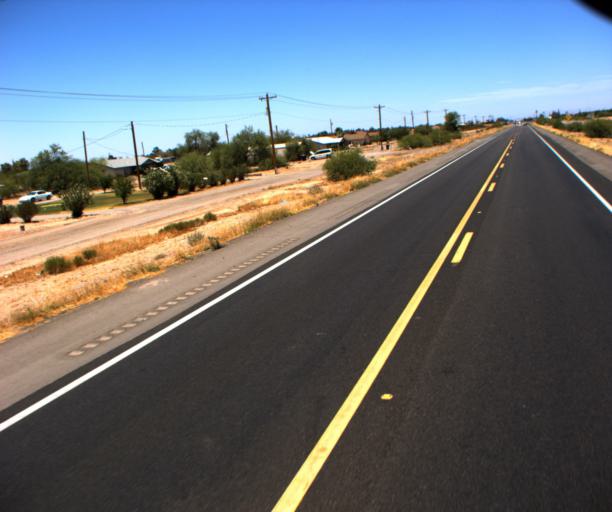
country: US
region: Arizona
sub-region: Maricopa County
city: Sun Lakes
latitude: 33.1953
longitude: -111.8409
